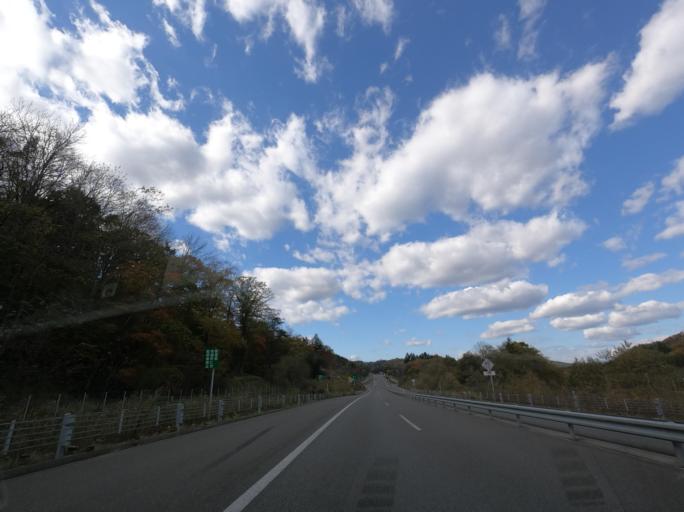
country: JP
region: Hokkaido
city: Kushiro
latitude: 43.0759
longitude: 144.0696
